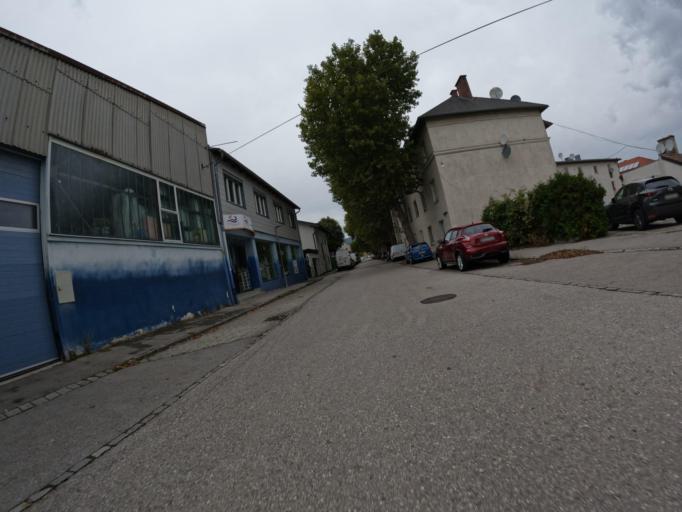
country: AT
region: Lower Austria
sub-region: Politischer Bezirk Baden
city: Traiskirchen
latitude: 48.0270
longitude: 16.3071
